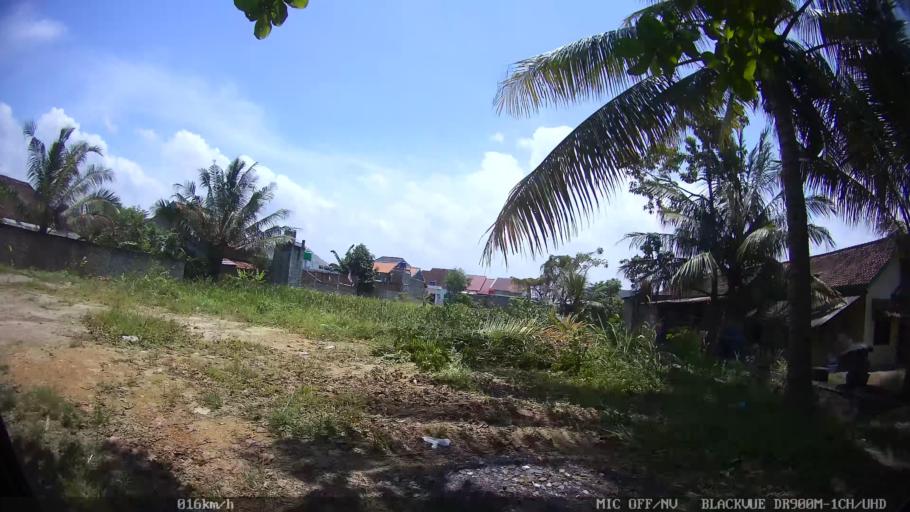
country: ID
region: Lampung
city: Kedaton
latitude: -5.3725
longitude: 105.2854
